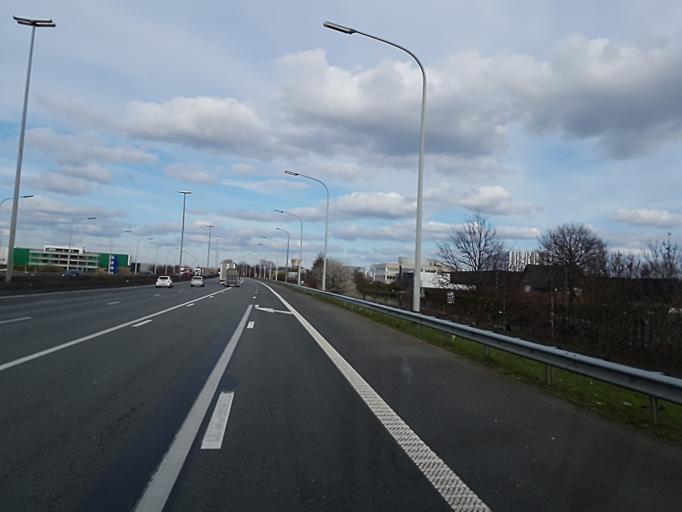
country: BE
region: Flanders
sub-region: Provincie Oost-Vlaanderen
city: Temse
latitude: 51.1427
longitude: 4.1830
